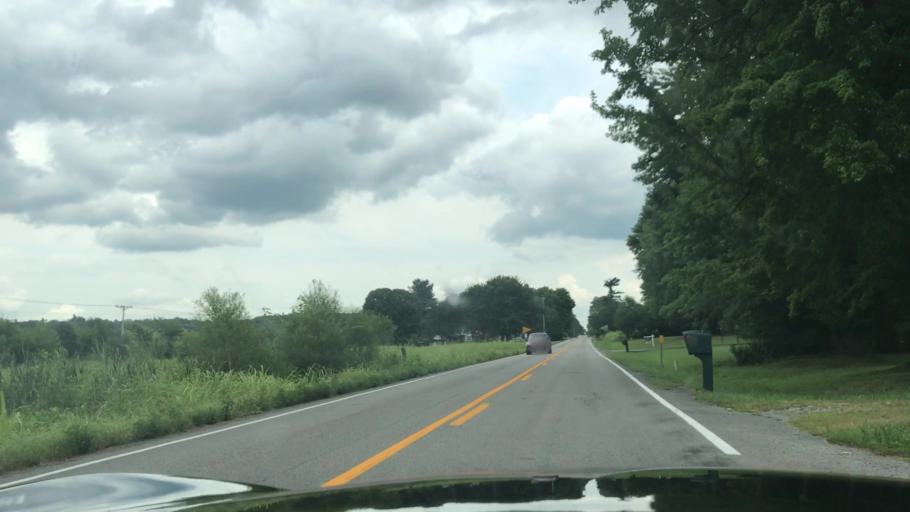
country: US
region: Kentucky
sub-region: Muhlenberg County
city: Central City
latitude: 37.2033
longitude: -87.0122
